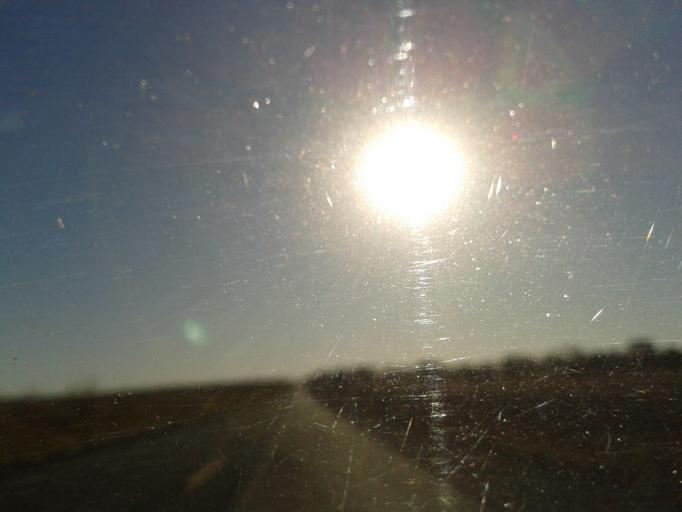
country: BR
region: Minas Gerais
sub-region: Santa Vitoria
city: Santa Vitoria
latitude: -19.1446
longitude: -50.1822
